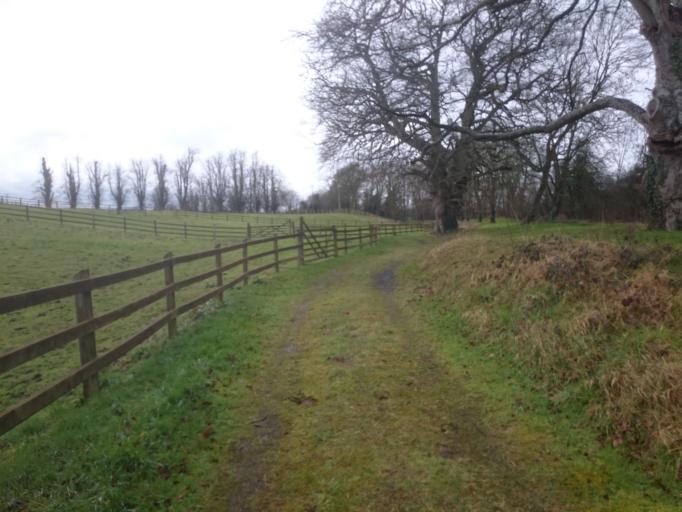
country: IE
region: Leinster
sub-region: Laois
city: Abbeyleix
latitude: 52.8470
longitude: -7.4006
